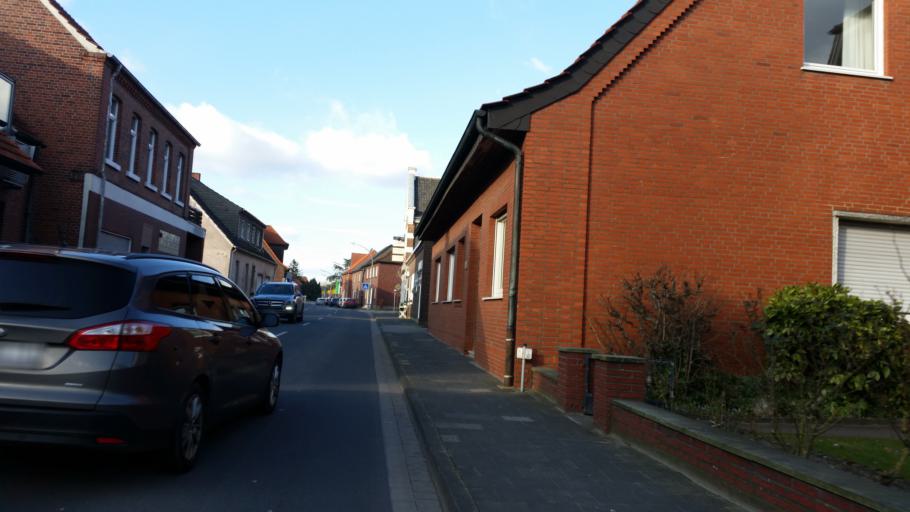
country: DE
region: North Rhine-Westphalia
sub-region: Regierungsbezirk Munster
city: Wettringen
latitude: 52.2111
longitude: 7.3192
